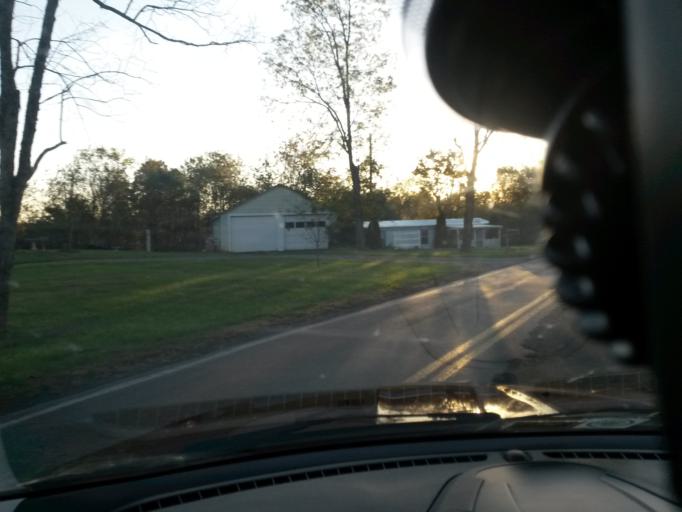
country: US
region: Virginia
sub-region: Roanoke County
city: Vinton
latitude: 37.1641
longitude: -79.8135
